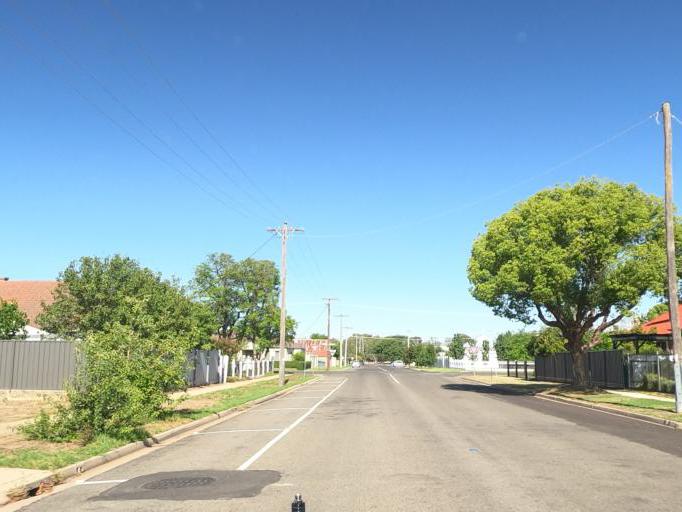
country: AU
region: Victoria
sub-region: Moira
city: Yarrawonga
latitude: -36.0131
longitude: 146.0025
